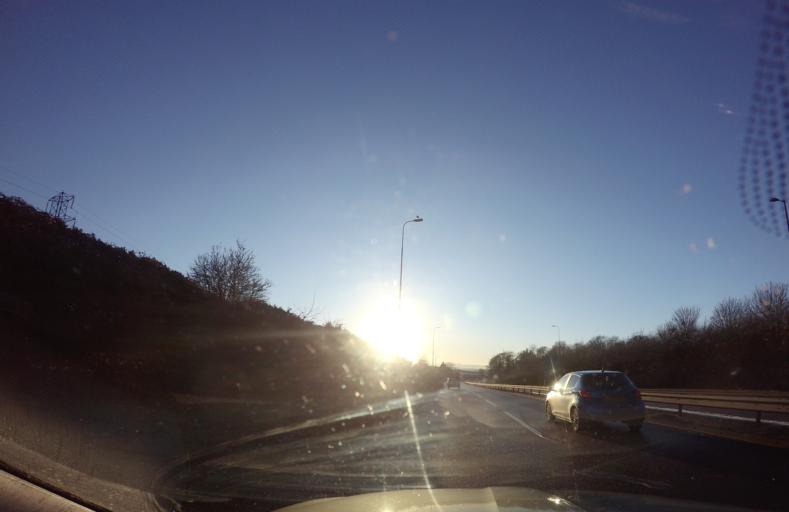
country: GB
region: Scotland
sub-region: Angus
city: Muirhead
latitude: 56.4794
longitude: -3.0255
